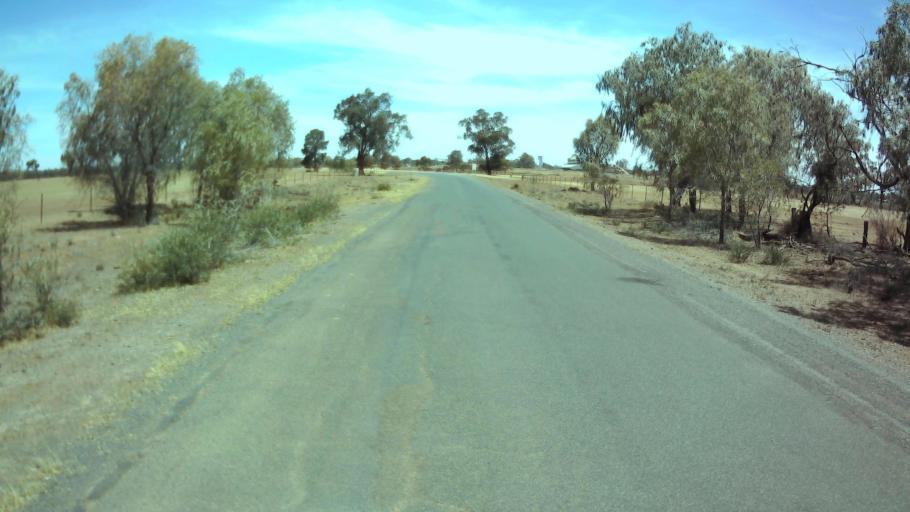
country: AU
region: New South Wales
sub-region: Weddin
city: Grenfell
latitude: -33.8301
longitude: 147.7458
